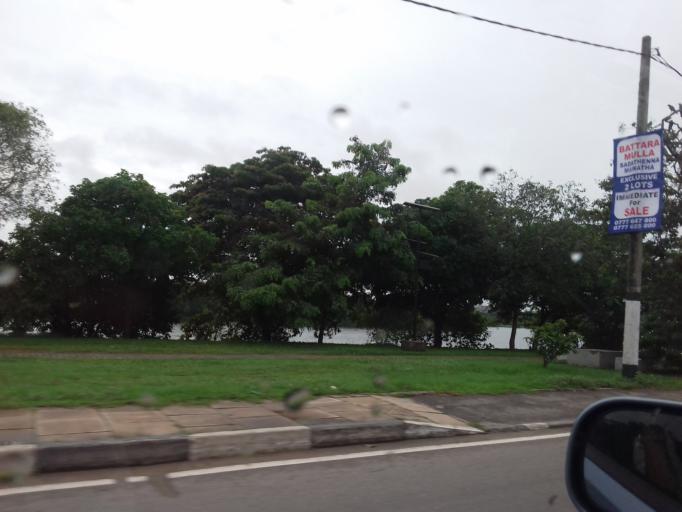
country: LK
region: Western
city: Pita Kotte
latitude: 6.9056
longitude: 79.9053
